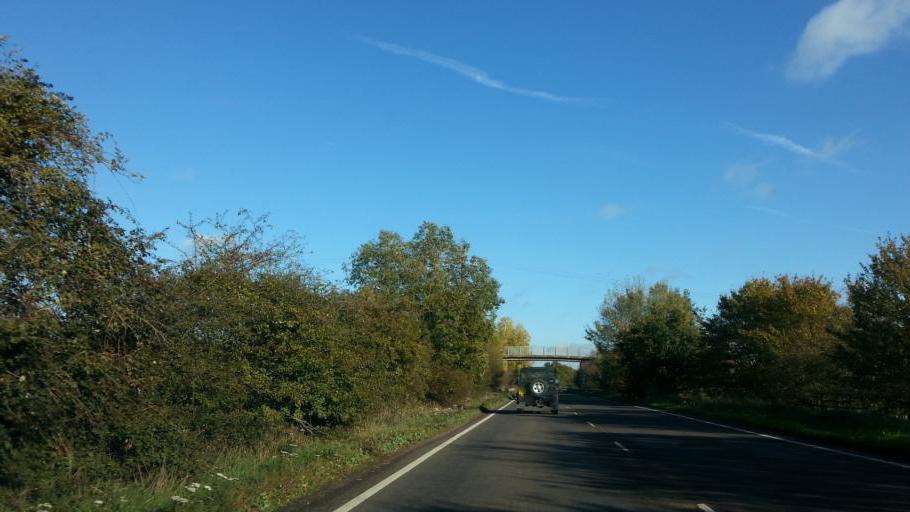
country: GB
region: England
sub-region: Suffolk
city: Bungay
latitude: 52.4307
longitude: 1.3695
